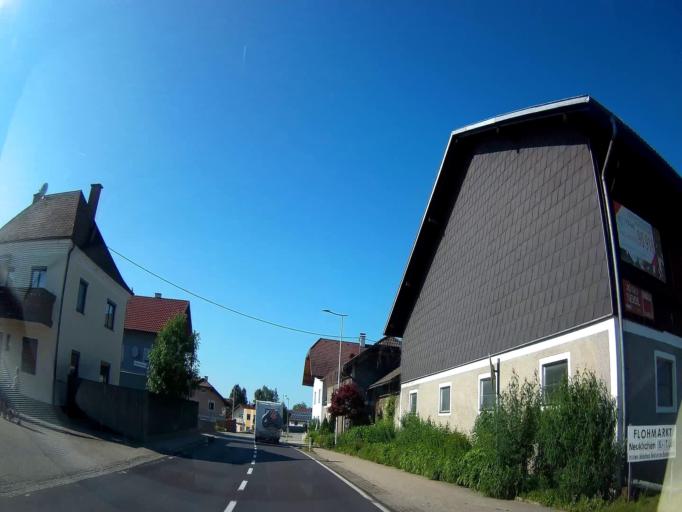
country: AT
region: Upper Austria
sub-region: Politischer Bezirk Braunau am Inn
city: Braunau am Inn
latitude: 48.1762
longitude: 13.0501
